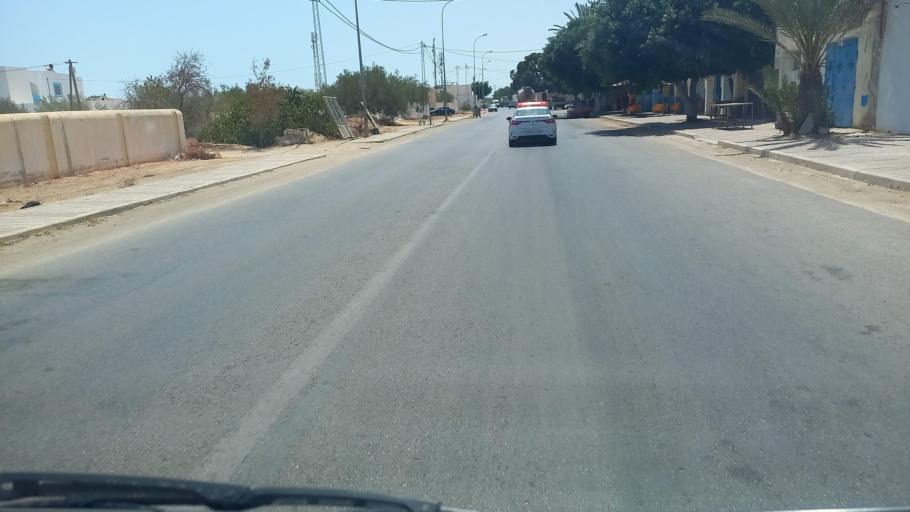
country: TN
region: Madanin
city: Midoun
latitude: 33.7773
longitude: 10.8931
